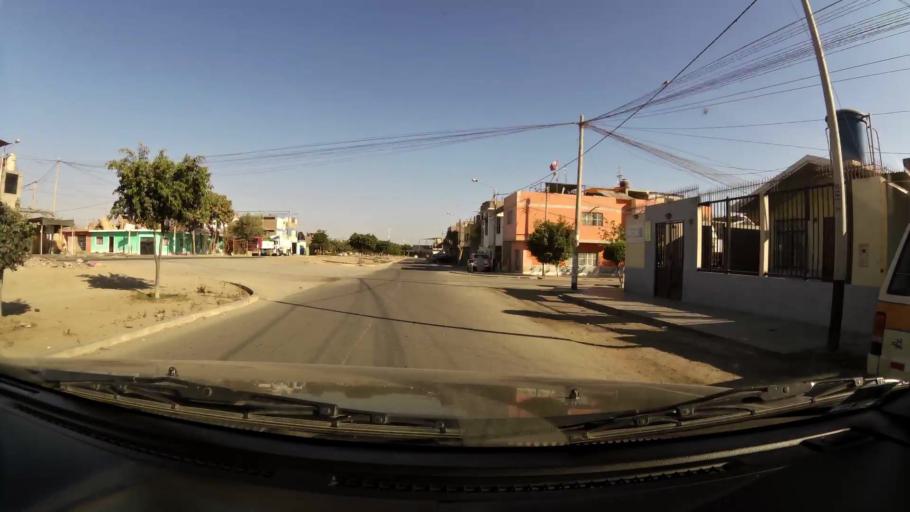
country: PE
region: Ica
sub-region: Provincia de Ica
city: La Tinguina
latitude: -14.0423
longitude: -75.7066
